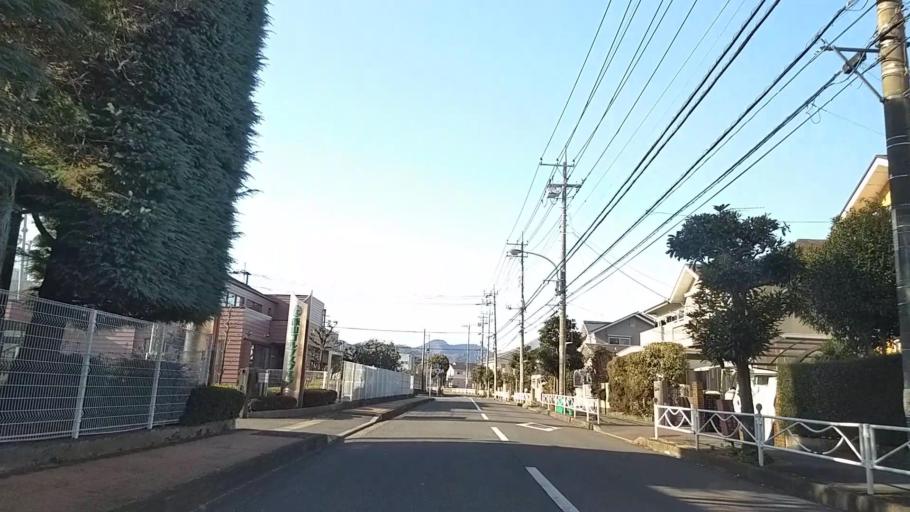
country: JP
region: Kanagawa
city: Atsugi
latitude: 35.4612
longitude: 139.3296
